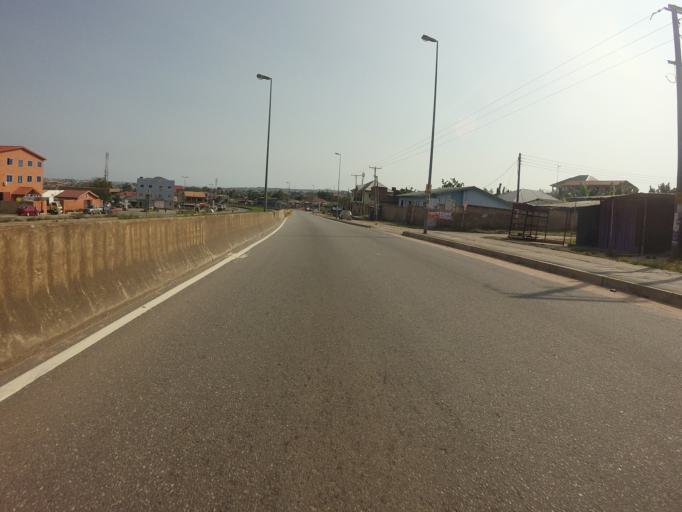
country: GH
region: Greater Accra
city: Gbawe
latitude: 5.6106
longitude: -0.2972
